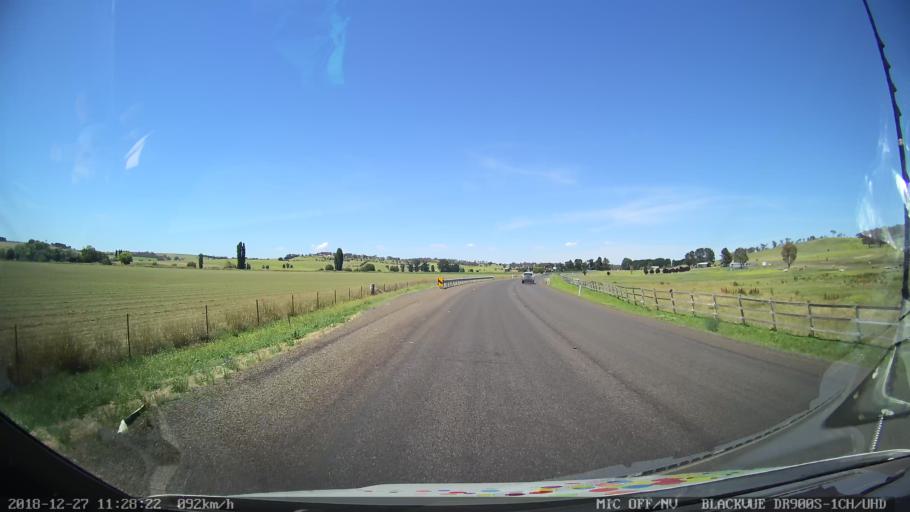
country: AU
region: New South Wales
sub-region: Bathurst Regional
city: Perthville
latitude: -33.4754
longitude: 149.5640
